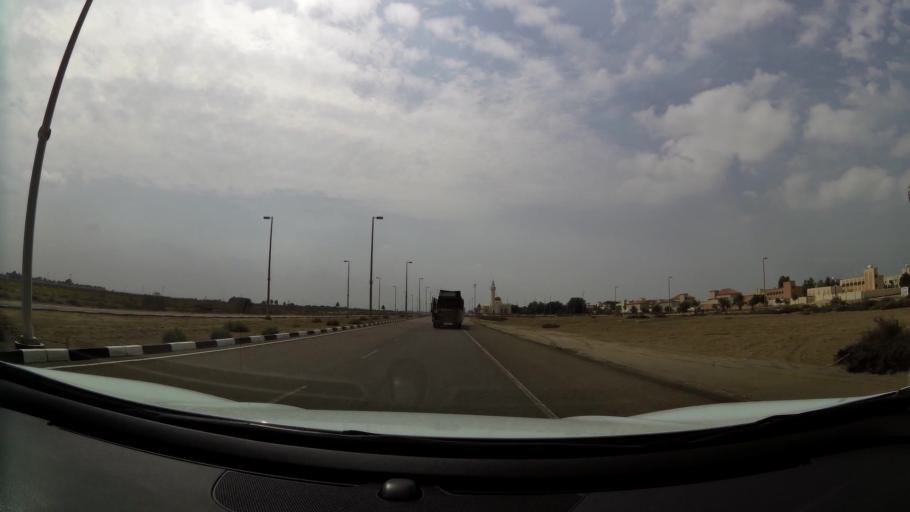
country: AE
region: Abu Dhabi
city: Abu Dhabi
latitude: 24.5981
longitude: 54.6518
